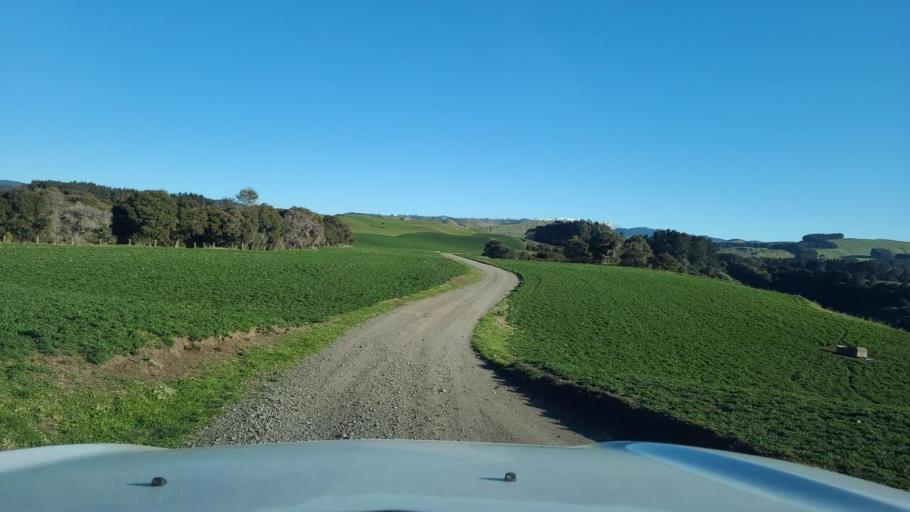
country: NZ
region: Hawke's Bay
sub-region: Napier City
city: Taradale
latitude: -39.4158
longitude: 176.5378
